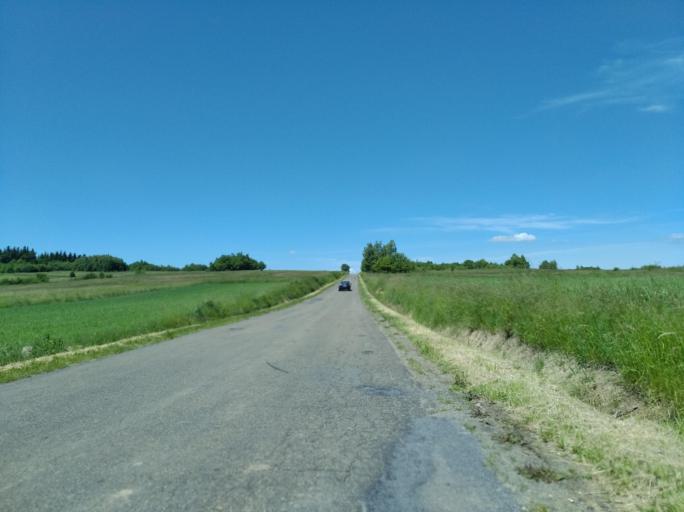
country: PL
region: Subcarpathian Voivodeship
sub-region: Powiat krosnienski
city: Chorkowka
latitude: 49.6406
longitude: 21.6301
